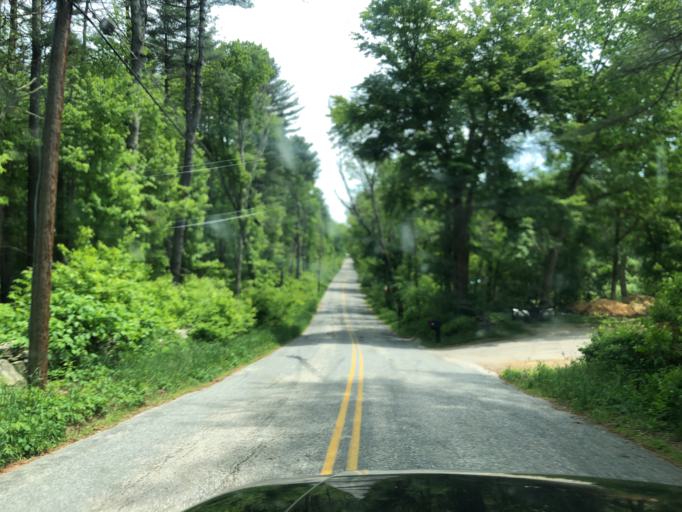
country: US
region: Connecticut
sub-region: Windham County
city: Thompson
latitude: 41.9652
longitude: -71.8297
